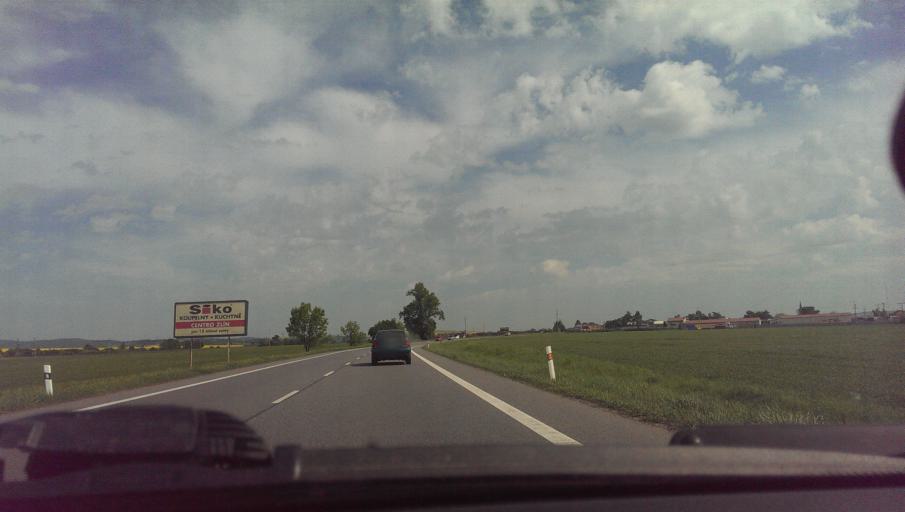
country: CZ
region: Zlin
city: Babice
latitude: 49.1017
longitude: 17.4563
